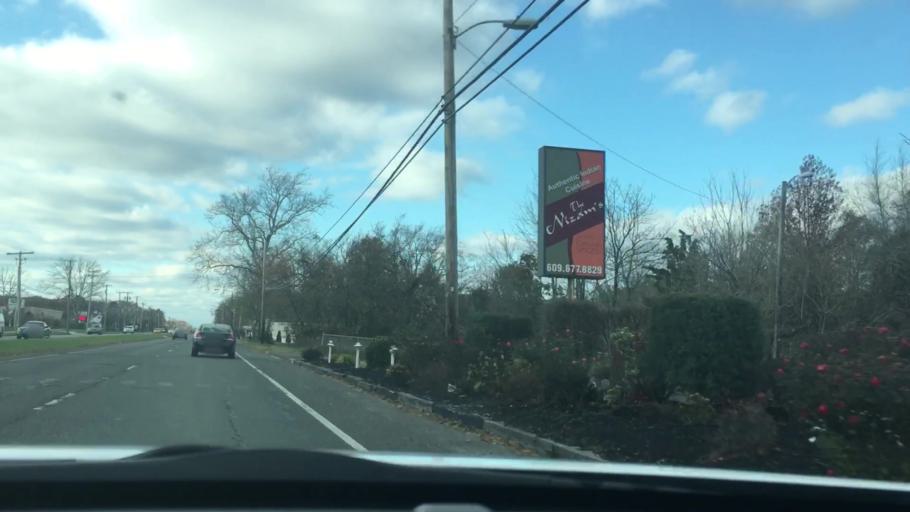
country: US
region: New Jersey
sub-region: Atlantic County
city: Northfield
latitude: 39.4117
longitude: -74.5709
